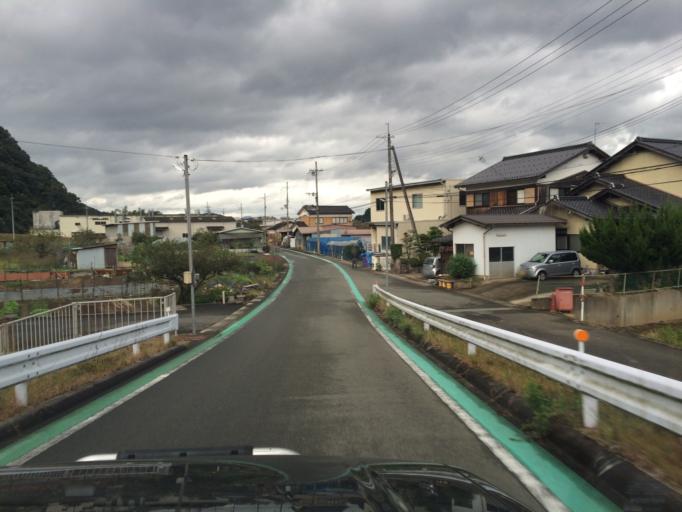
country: JP
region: Hyogo
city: Toyooka
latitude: 35.4581
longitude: 134.7700
